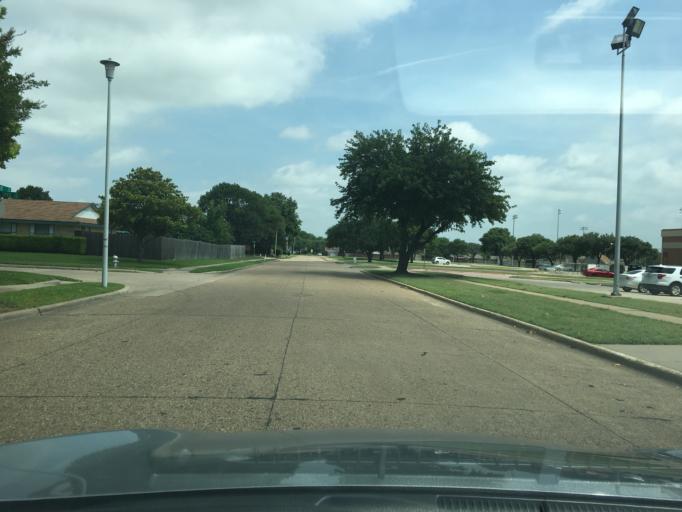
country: US
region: Texas
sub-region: Dallas County
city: Garland
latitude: 32.9249
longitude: -96.6792
